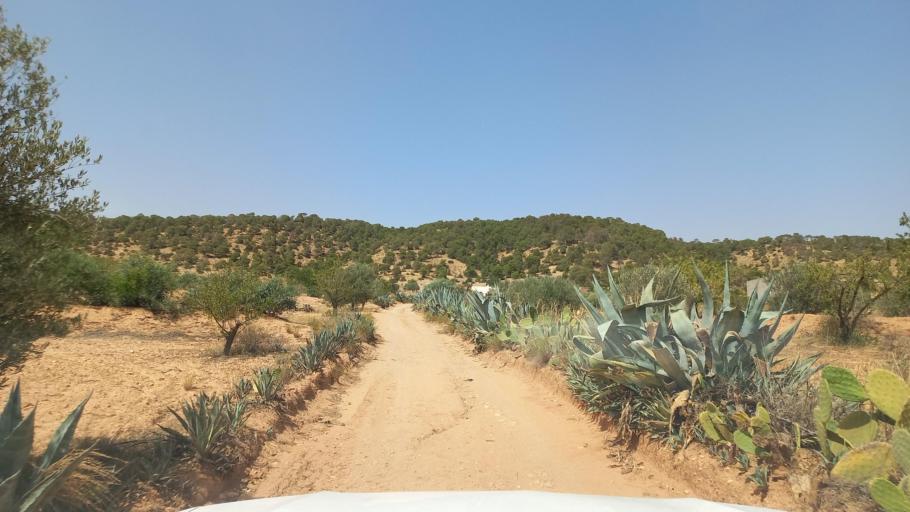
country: TN
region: Al Qasrayn
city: Kasserine
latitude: 35.3766
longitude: 8.9084
